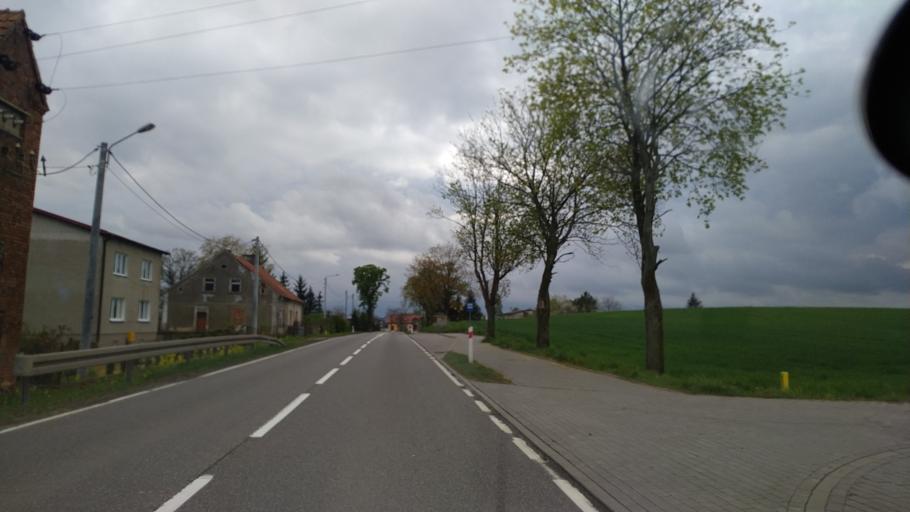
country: PL
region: Pomeranian Voivodeship
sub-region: Powiat kwidzynski
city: Kwidzyn
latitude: 53.7728
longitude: 18.9508
